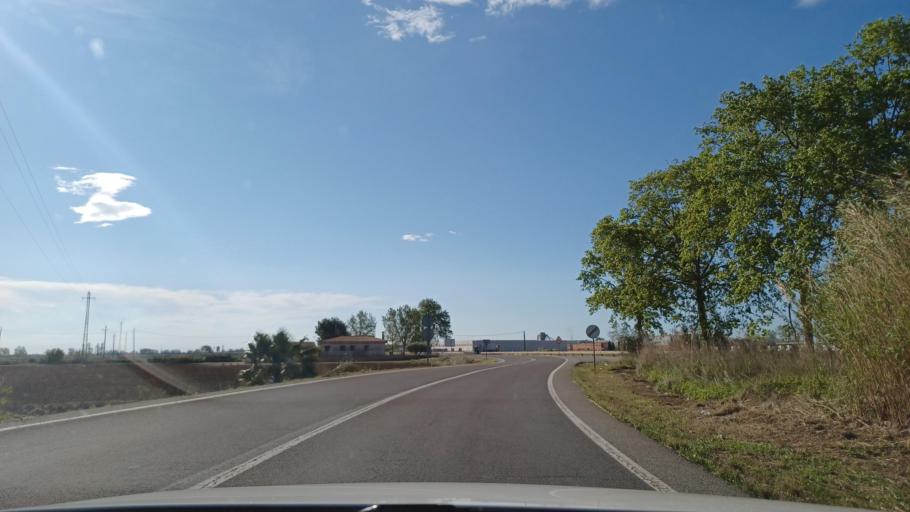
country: ES
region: Catalonia
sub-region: Provincia de Tarragona
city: Amposta
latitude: 40.7187
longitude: 0.5867
